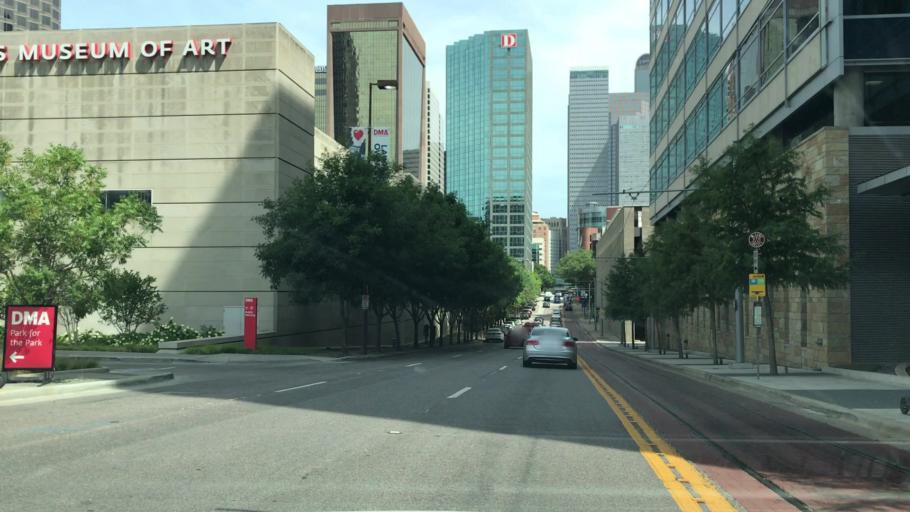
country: US
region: Texas
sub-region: Dallas County
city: Dallas
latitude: 32.7880
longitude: -96.8023
